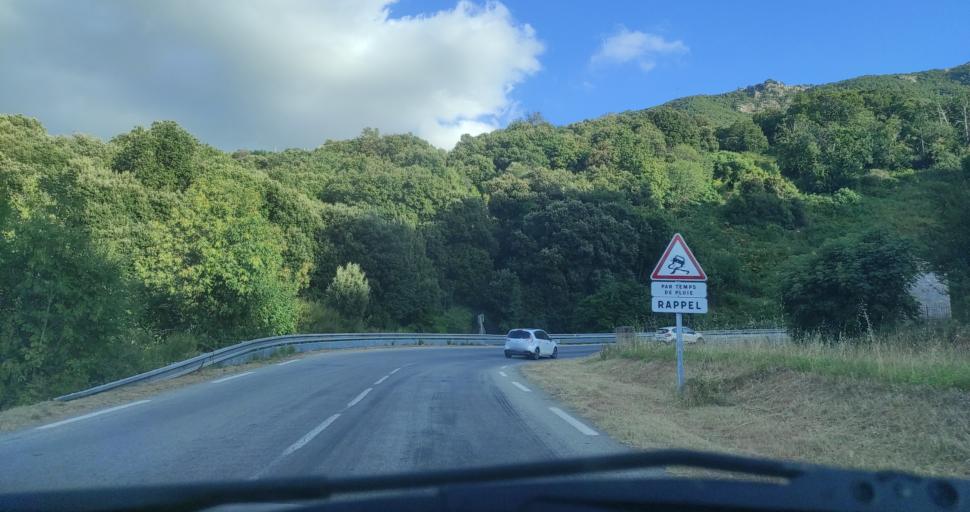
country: FR
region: Corsica
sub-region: Departement de la Corse-du-Sud
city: Appietto
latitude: 42.0319
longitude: 8.7652
